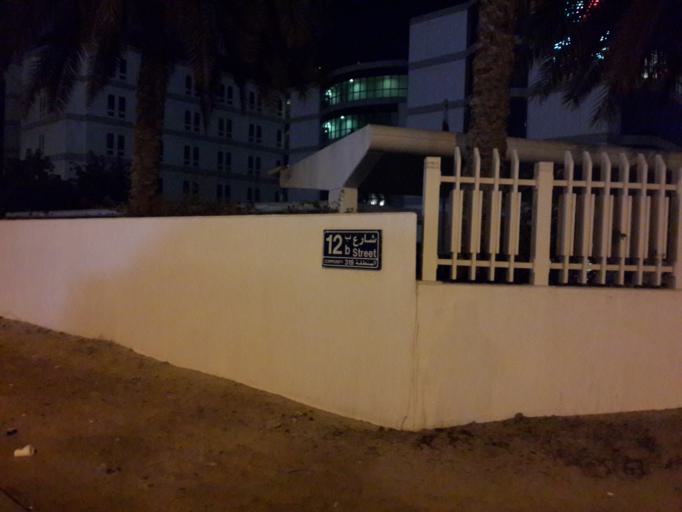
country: AE
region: Ash Shariqah
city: Sharjah
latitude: 25.2341
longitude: 55.3112
